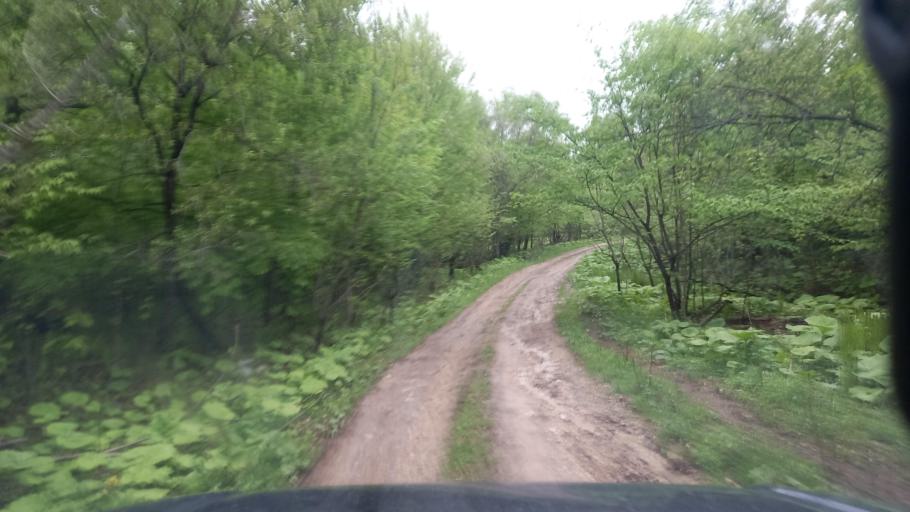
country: RU
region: Kabardino-Balkariya
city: Babugent
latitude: 43.2185
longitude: 43.5528
